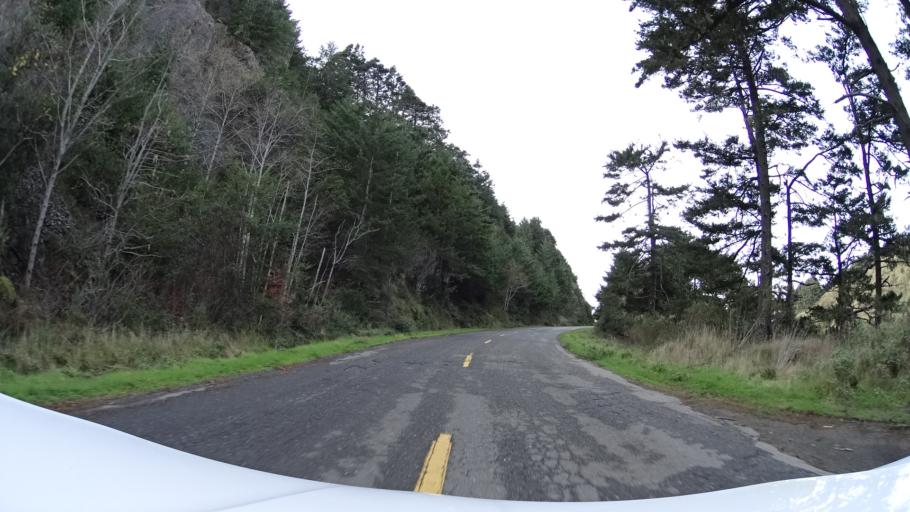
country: US
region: California
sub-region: Humboldt County
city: Ferndale
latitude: 40.3473
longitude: -124.3535
